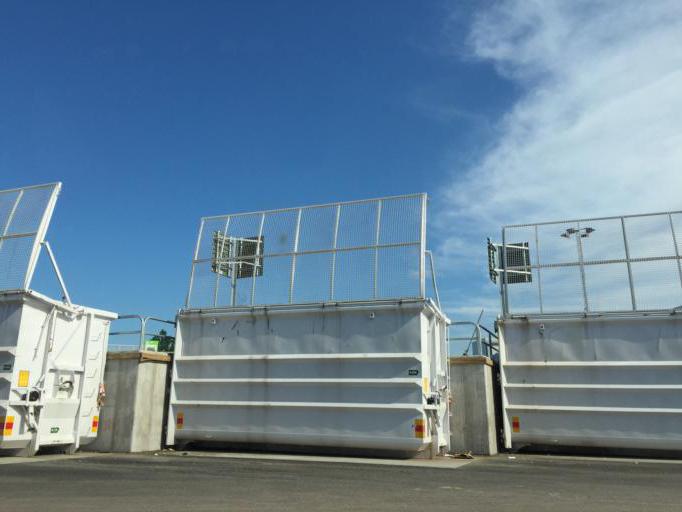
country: SE
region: Soedermanland
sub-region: Eskilstuna Kommun
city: Hallbybrunn
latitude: 59.3900
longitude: 16.4512
